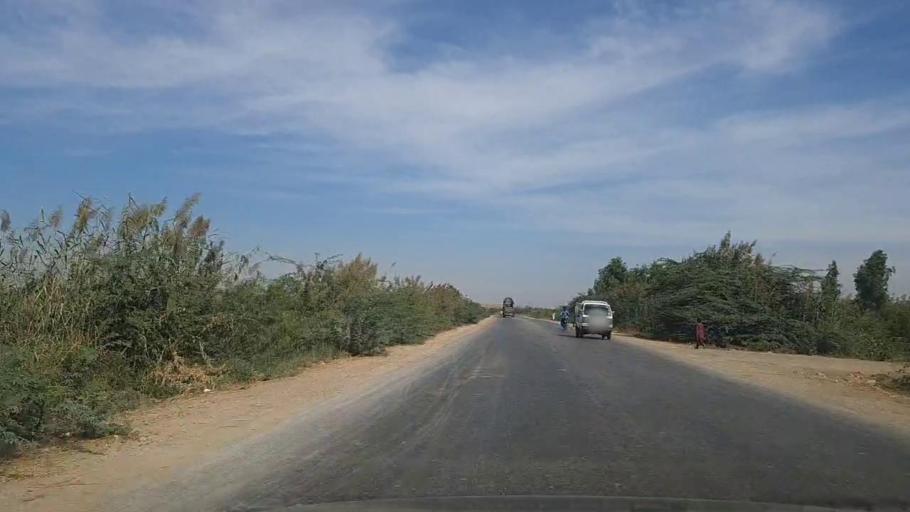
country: PK
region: Sindh
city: Daro Mehar
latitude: 24.9792
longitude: 68.1302
